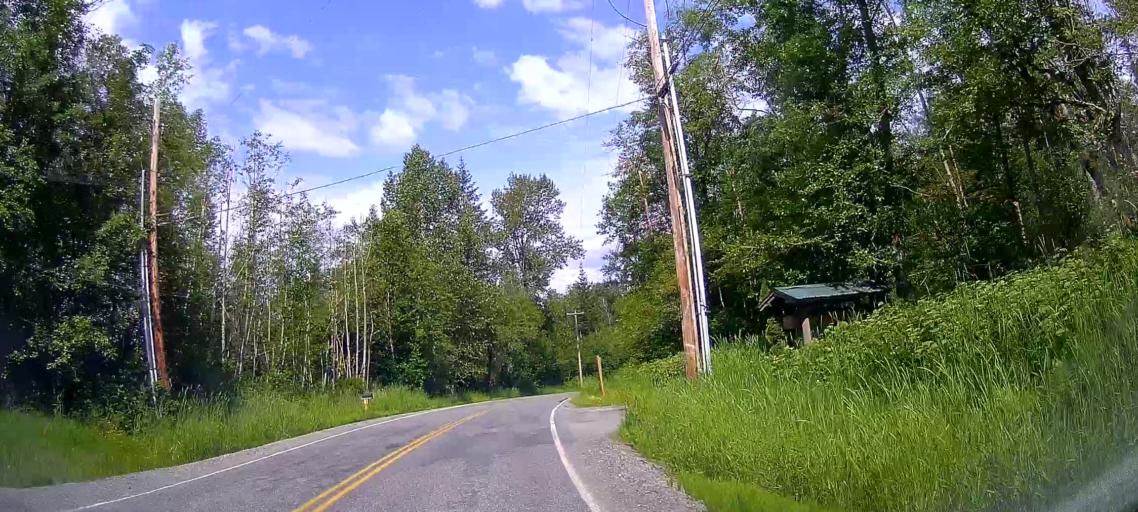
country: US
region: Washington
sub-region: Skagit County
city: Burlington
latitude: 48.5733
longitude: -122.3832
